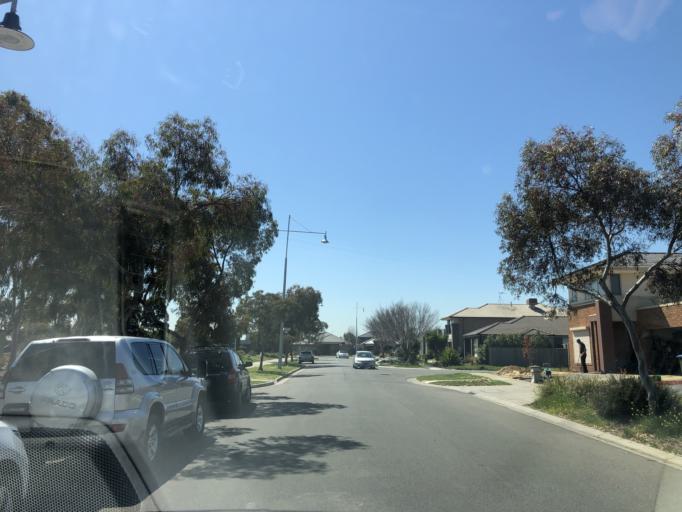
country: AU
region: Victoria
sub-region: Wyndham
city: Point Cook
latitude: -37.8999
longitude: 144.7314
